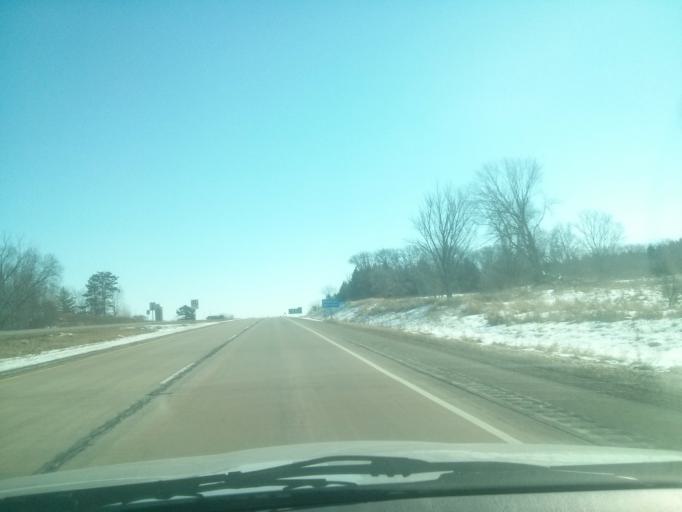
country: US
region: Wisconsin
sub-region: Saint Croix County
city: New Richmond
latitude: 45.1226
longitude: -92.6013
